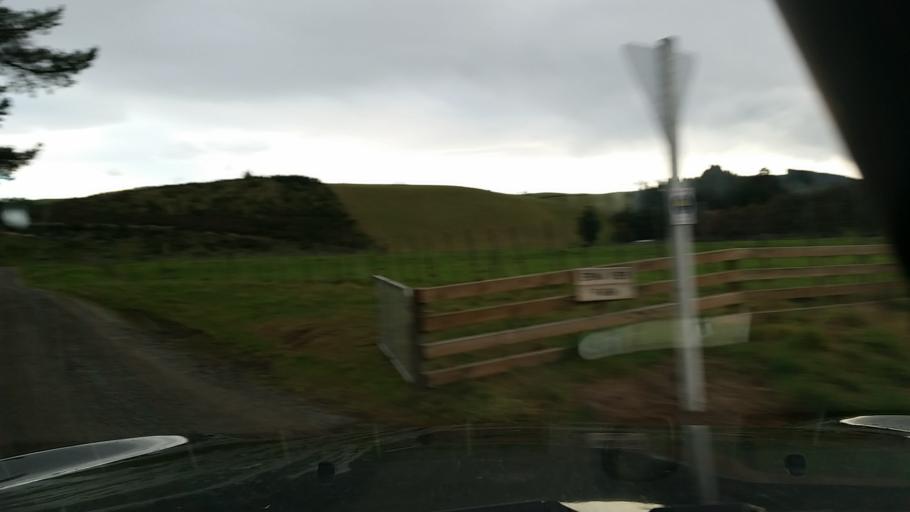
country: NZ
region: Marlborough
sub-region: Marlborough District
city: Blenheim
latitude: -41.5417
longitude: 173.6065
